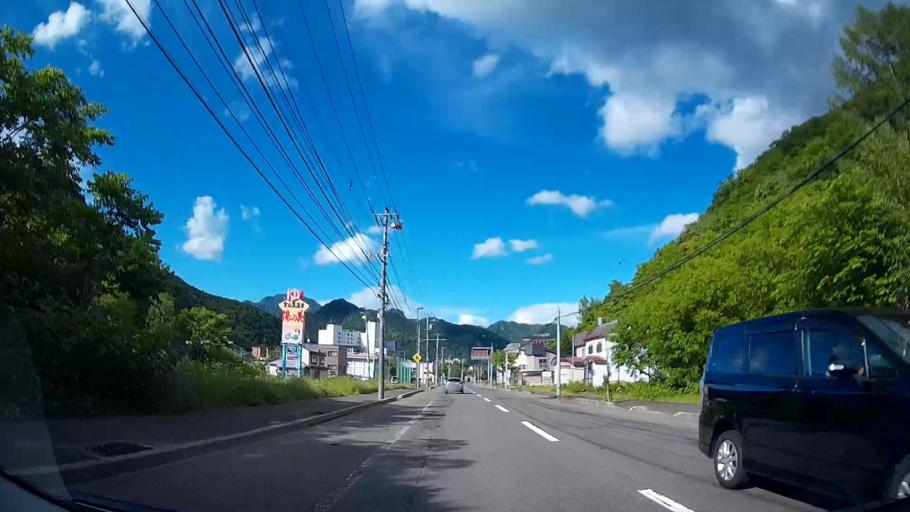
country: JP
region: Hokkaido
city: Sapporo
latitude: 42.9605
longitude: 141.1576
